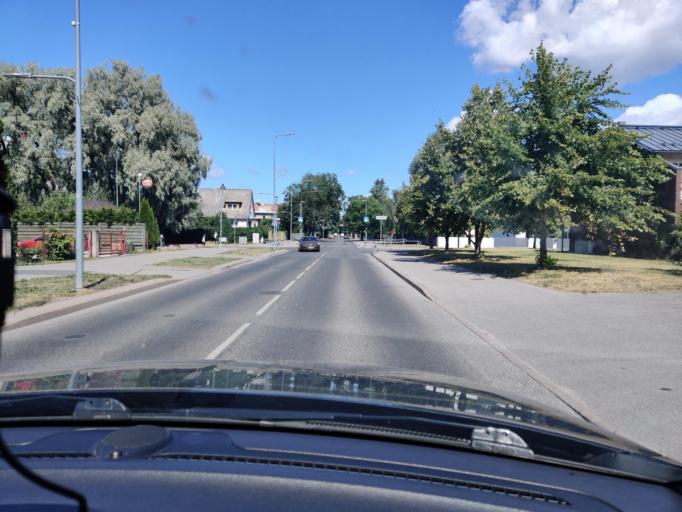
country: EE
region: Harju
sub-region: Tallinna linn
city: Tallinn
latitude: 59.4090
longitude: 24.7132
